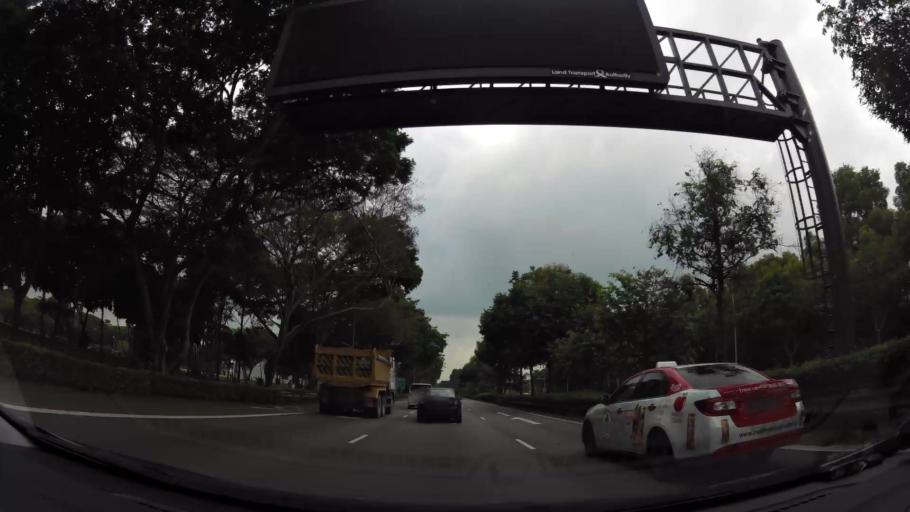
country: SG
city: Singapore
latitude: 1.3428
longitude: 103.9695
